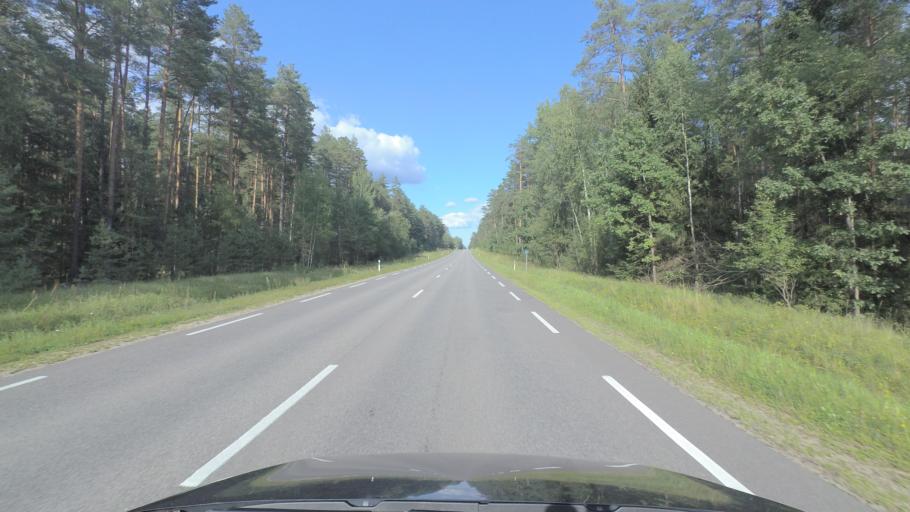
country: LT
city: Pabrade
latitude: 54.9546
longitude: 25.6753
